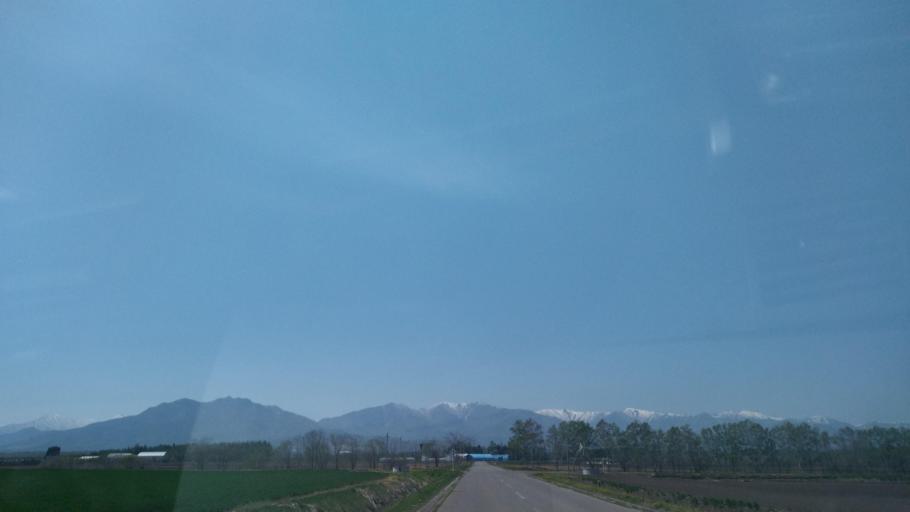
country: JP
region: Hokkaido
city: Obihiro
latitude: 42.8931
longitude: 143.0125
